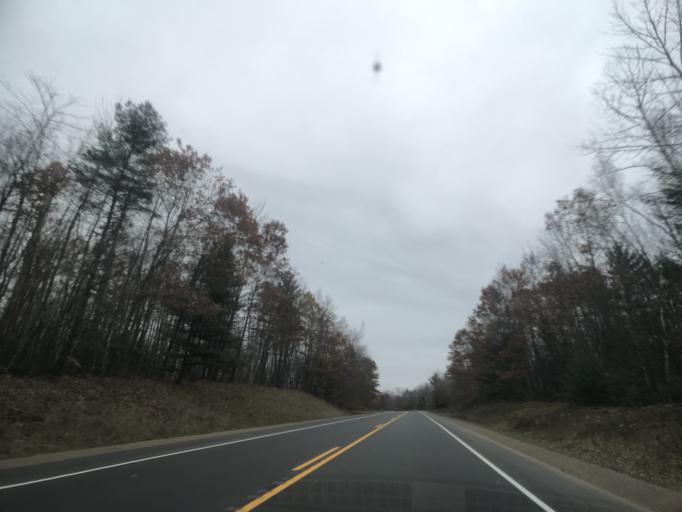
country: US
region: Wisconsin
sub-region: Menominee County
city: Legend Lake
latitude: 45.2690
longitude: -88.5099
